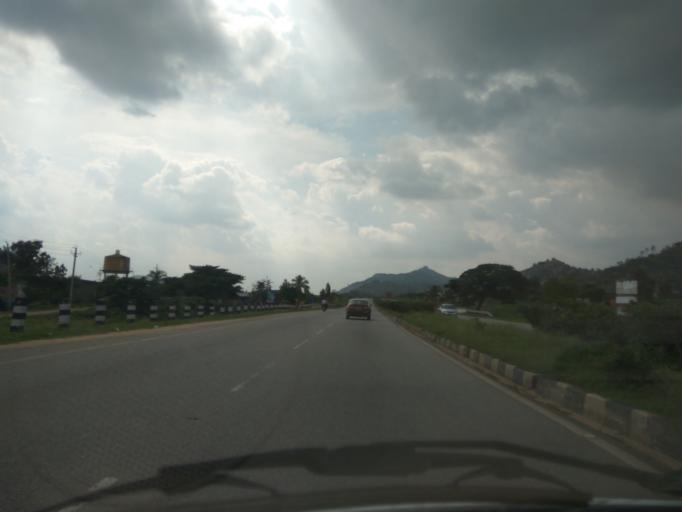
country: IN
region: Karnataka
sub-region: Kolar
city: Kolar
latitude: 13.1193
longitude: 78.0809
